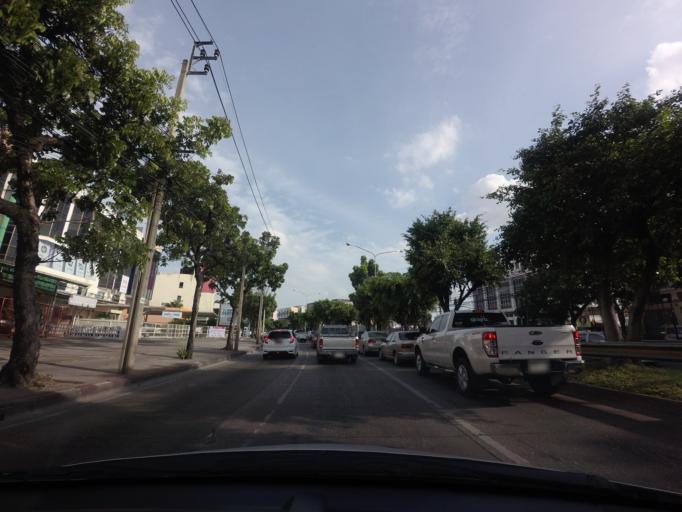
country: TH
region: Bangkok
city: Bueng Kum
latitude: 13.8042
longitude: 100.6475
